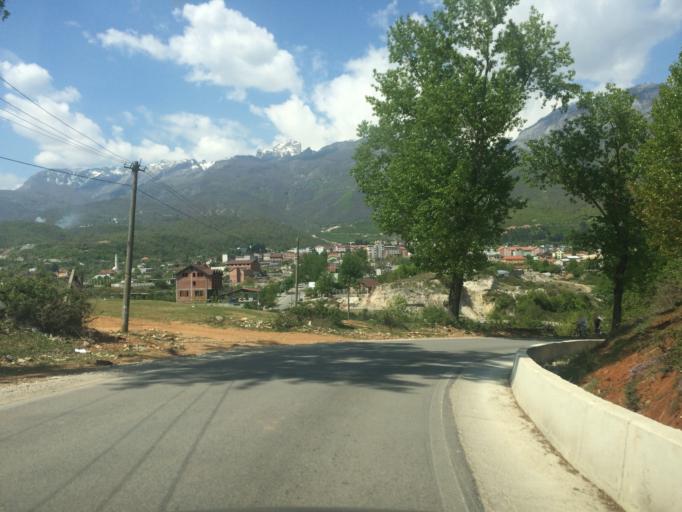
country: AL
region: Kukes
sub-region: Rrethi i Tropojes
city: Bajram Curri
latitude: 42.3571
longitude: 20.0866
